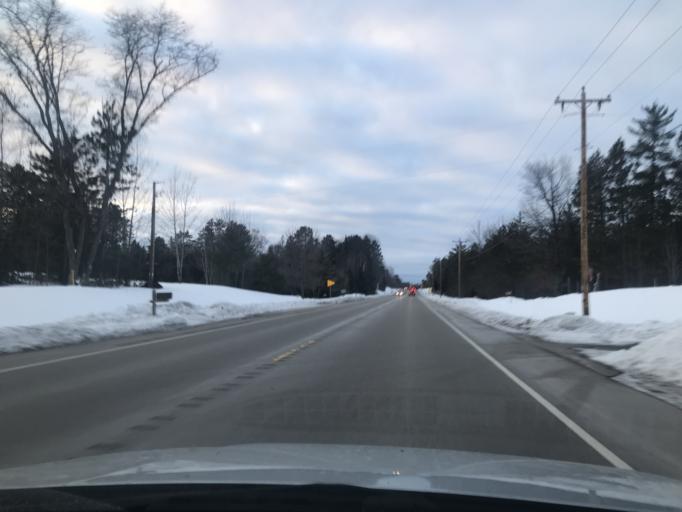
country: US
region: Wisconsin
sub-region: Marinette County
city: Marinette
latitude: 45.1565
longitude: -87.7140
